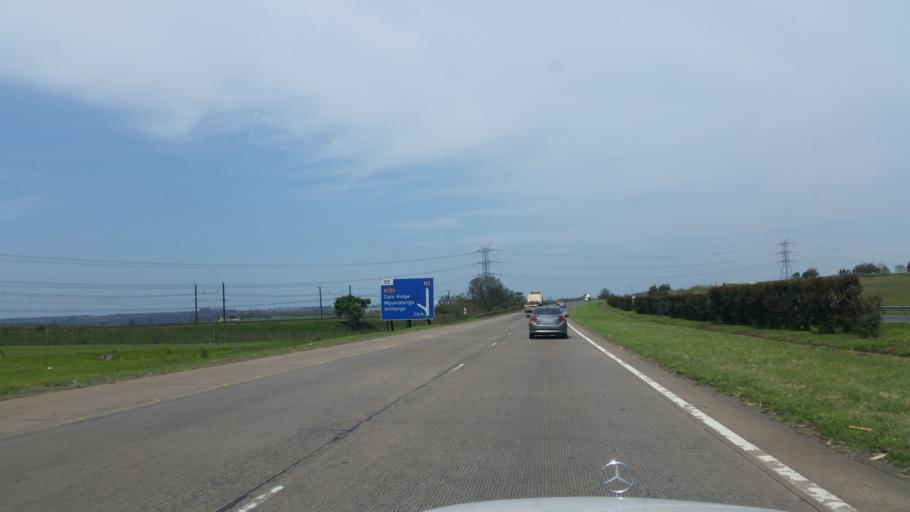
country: ZA
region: KwaZulu-Natal
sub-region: uMgungundlovu District Municipality
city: Camperdown
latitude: -29.7305
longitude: 30.5618
